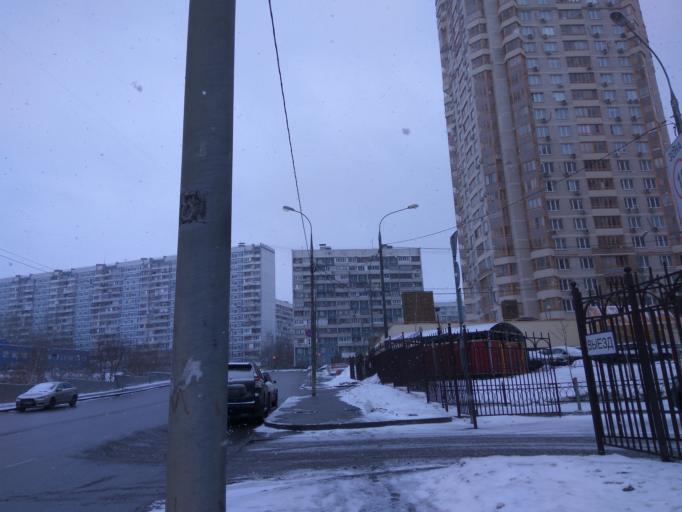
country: RU
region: Moscow
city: Strogino
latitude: 55.7933
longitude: 37.3969
